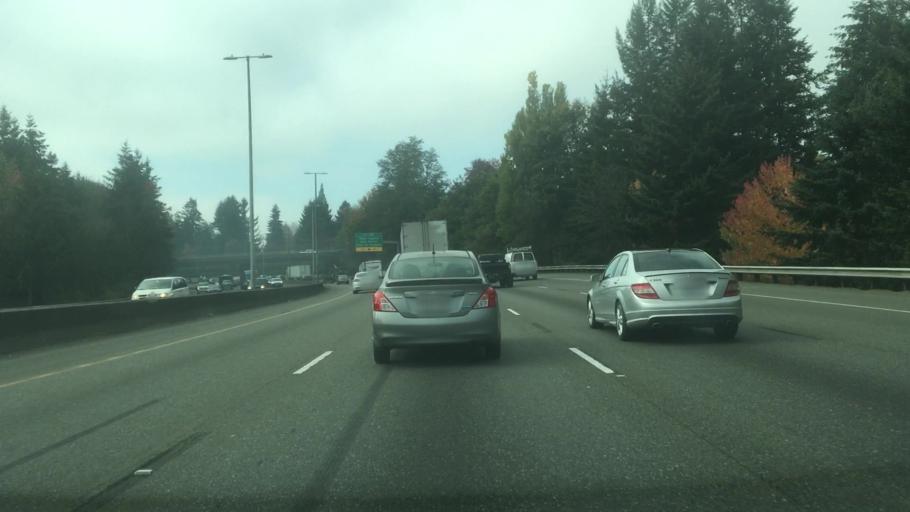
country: US
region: Washington
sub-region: Thurston County
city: Olympia
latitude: 47.0407
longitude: -122.8659
